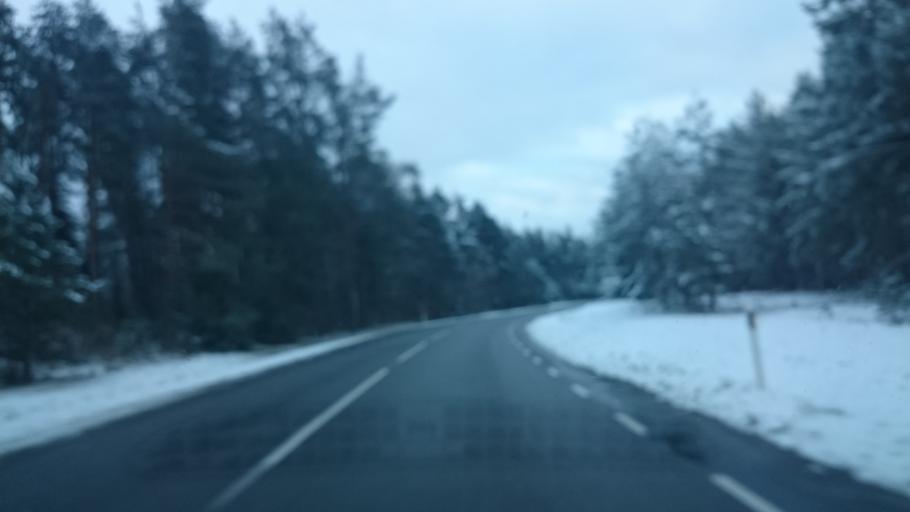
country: EE
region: Saare
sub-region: Kuressaare linn
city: Kuressaare
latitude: 58.3900
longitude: 22.6486
